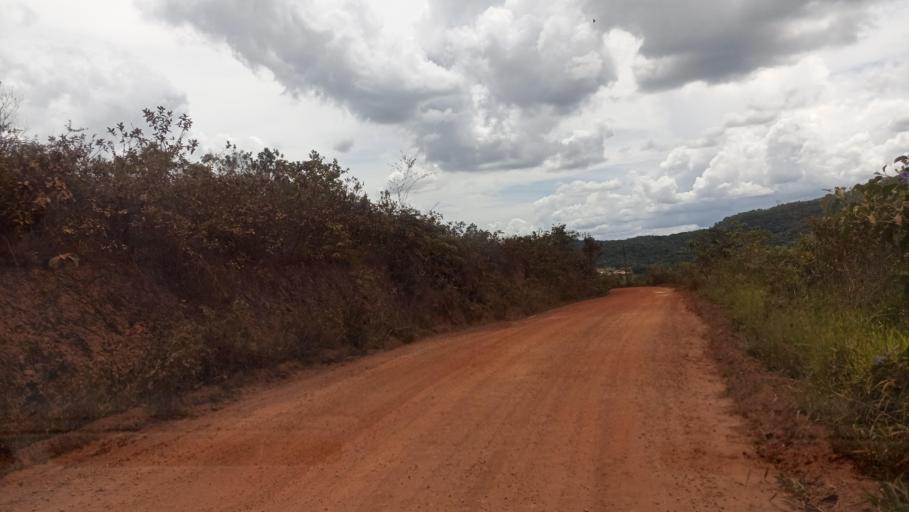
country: BR
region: Minas Gerais
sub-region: Itabirito
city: Itabirito
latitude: -20.3425
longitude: -43.7528
